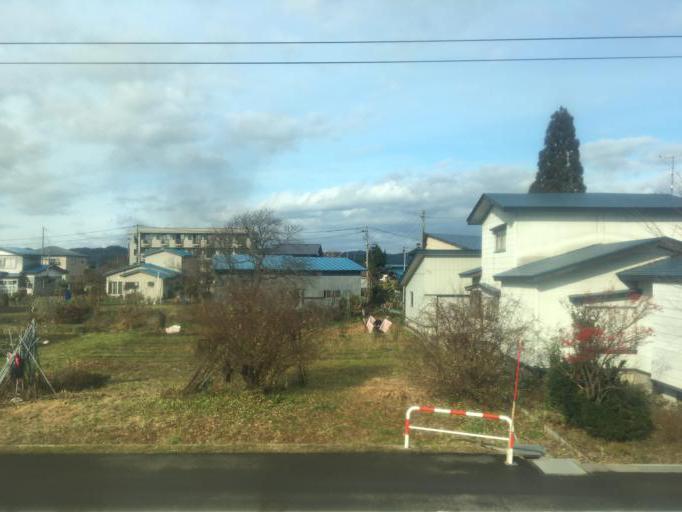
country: JP
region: Akita
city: Takanosu
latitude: 40.2359
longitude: 140.3801
